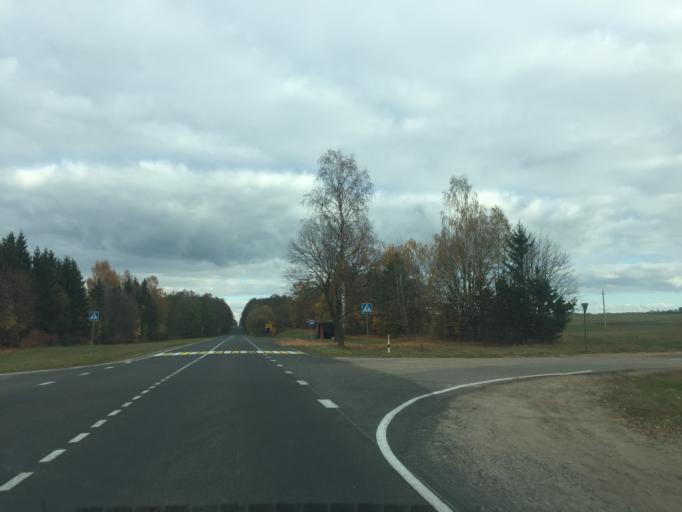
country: BY
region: Minsk
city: Svir
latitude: 54.8964
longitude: 26.4041
